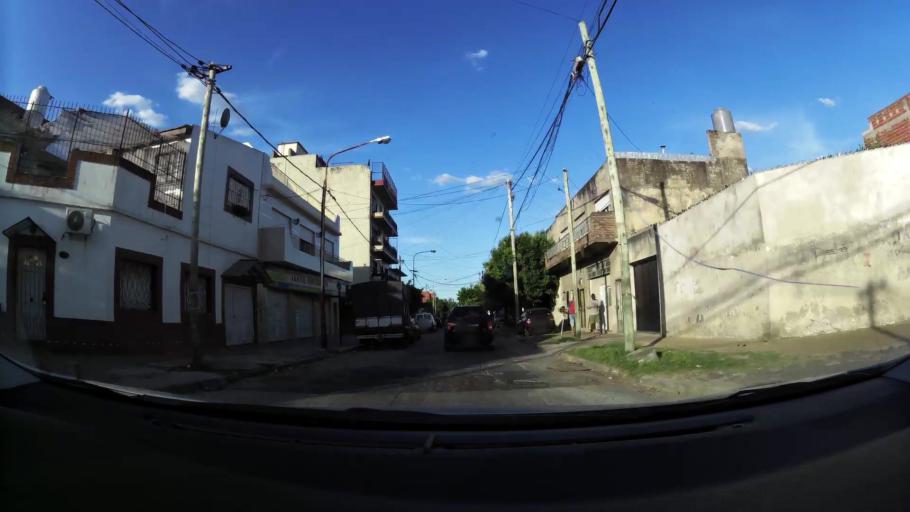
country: AR
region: Buenos Aires F.D.
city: Villa Lugano
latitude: -34.6922
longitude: -58.4869
